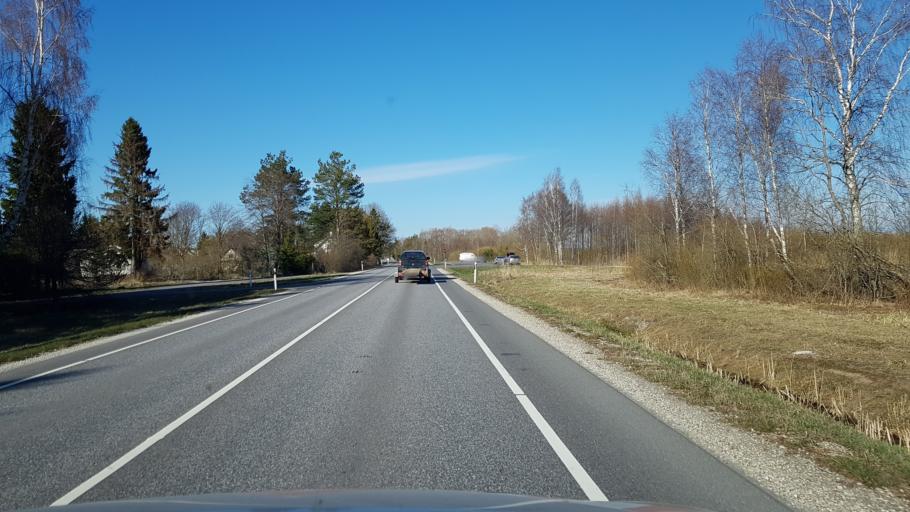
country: EE
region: Jogevamaa
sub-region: Mustvee linn
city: Mustvee
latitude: 58.9177
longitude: 27.0074
